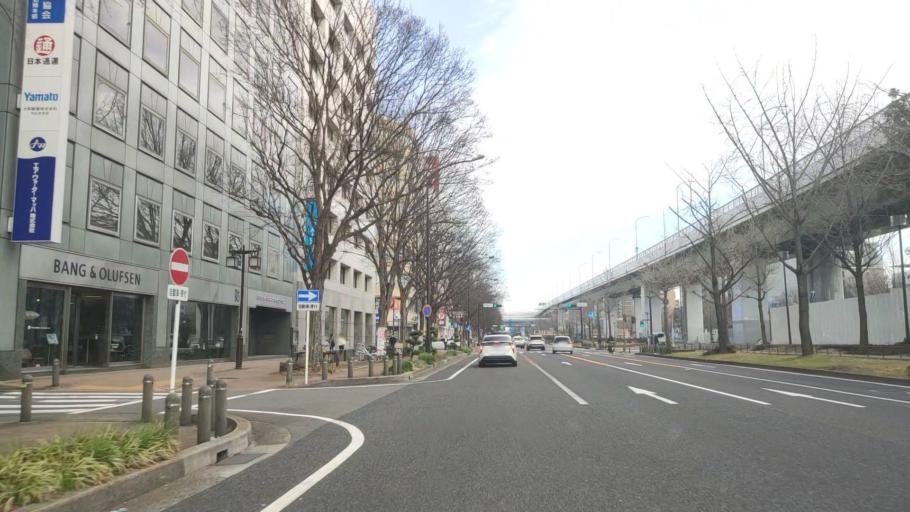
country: JP
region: Aichi
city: Nagoya-shi
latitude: 35.1623
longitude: 136.9102
